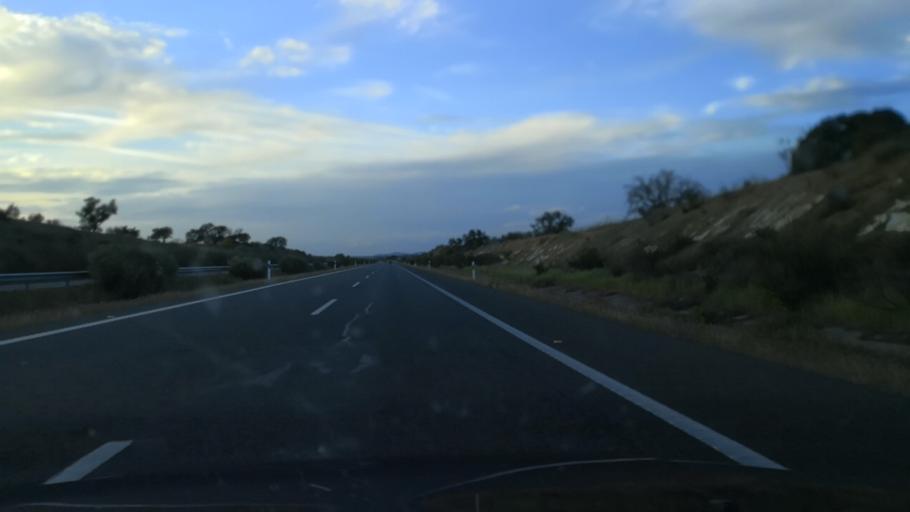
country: ES
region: Extremadura
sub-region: Provincia de Caceres
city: Casas de Don Antonio
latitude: 39.2050
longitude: -6.2831
